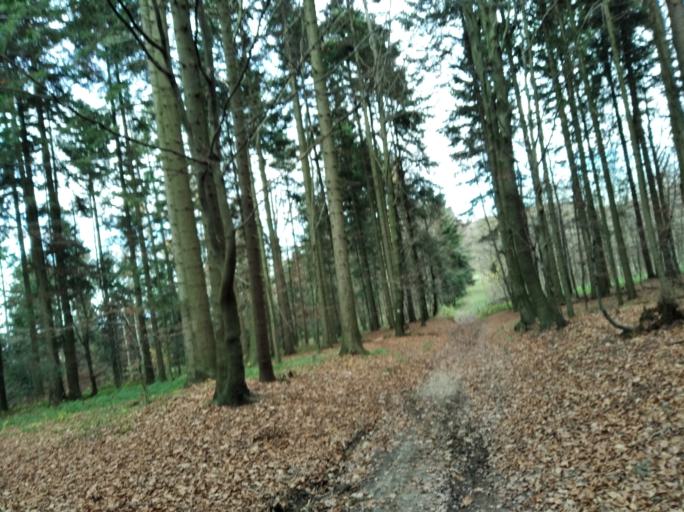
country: PL
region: Subcarpathian Voivodeship
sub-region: Powiat strzyzowski
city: Jawornik
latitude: 49.8647
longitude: 21.8557
